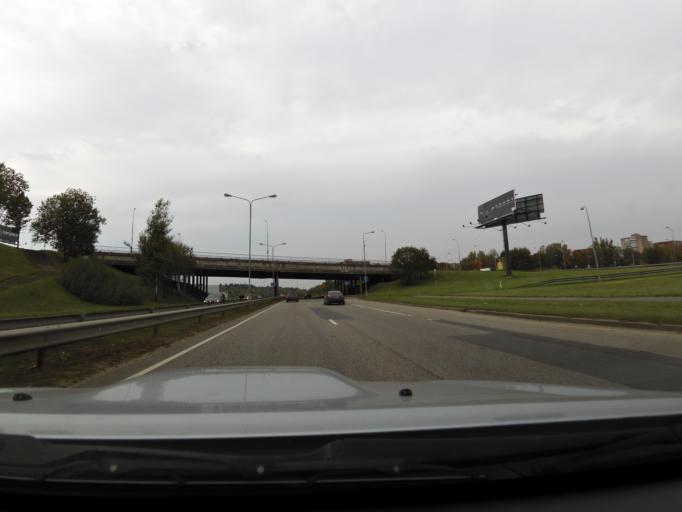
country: LT
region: Vilnius County
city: Naujamiestis
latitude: 54.6561
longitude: 25.2735
